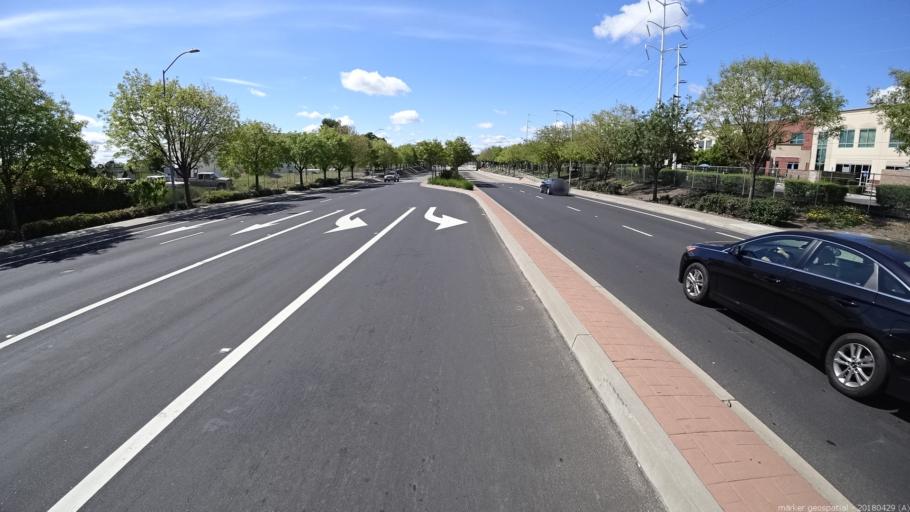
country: US
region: California
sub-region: Yolo County
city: West Sacramento
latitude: 38.5887
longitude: -121.5460
